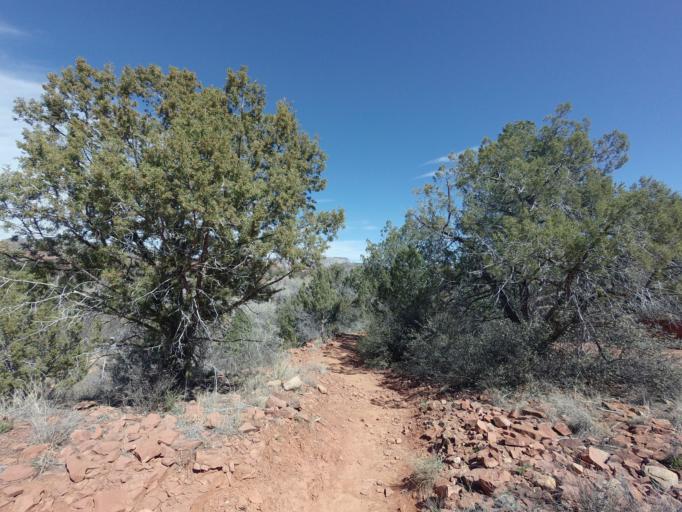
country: US
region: Arizona
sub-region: Yavapai County
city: West Sedona
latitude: 34.8088
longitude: -111.8250
